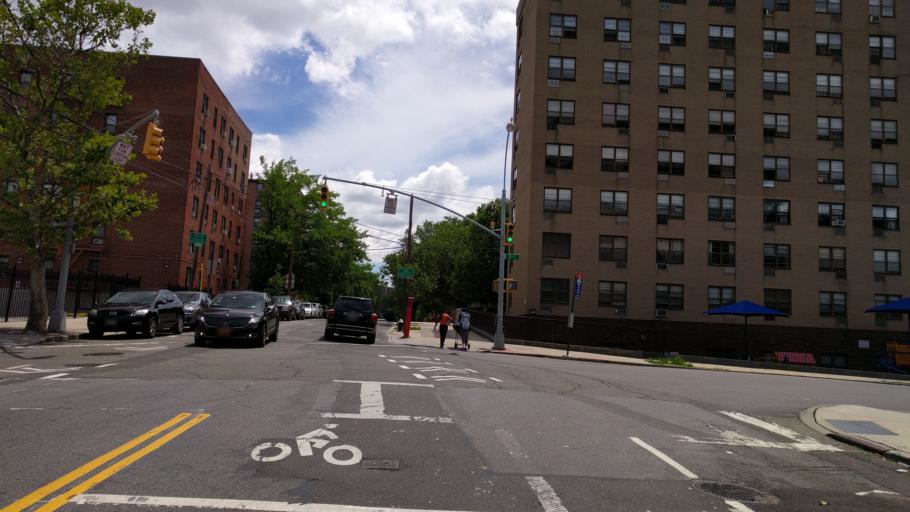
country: US
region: New York
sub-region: Queens County
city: Long Island City
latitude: 40.7743
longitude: -73.9321
